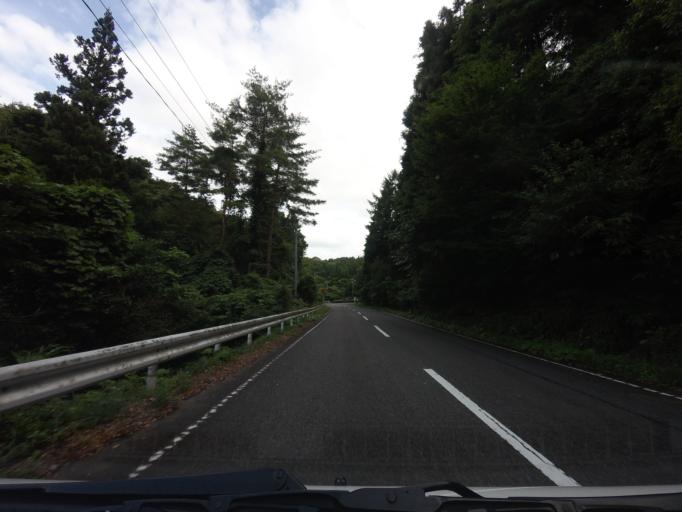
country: JP
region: Fukushima
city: Motomiya
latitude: 37.5434
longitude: 140.3219
